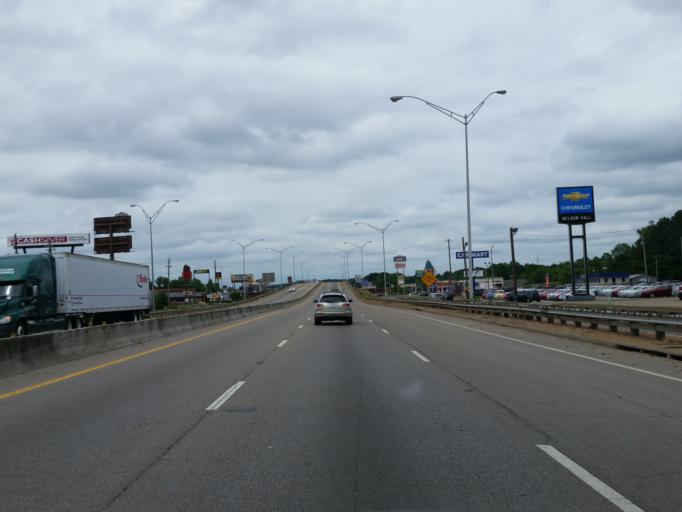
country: US
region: Mississippi
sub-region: Lauderdale County
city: Meridian
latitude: 32.3557
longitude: -88.6875
